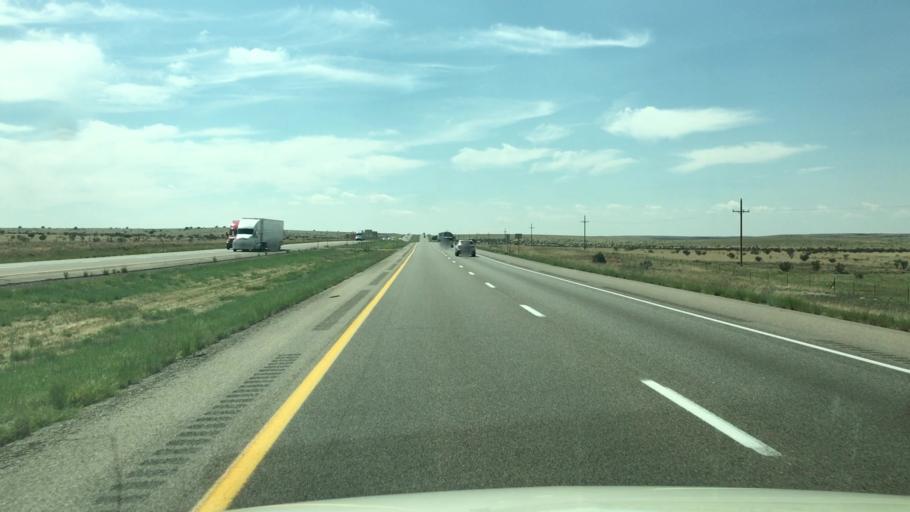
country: US
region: New Mexico
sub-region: Guadalupe County
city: Santa Rosa
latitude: 34.9786
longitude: -105.0309
